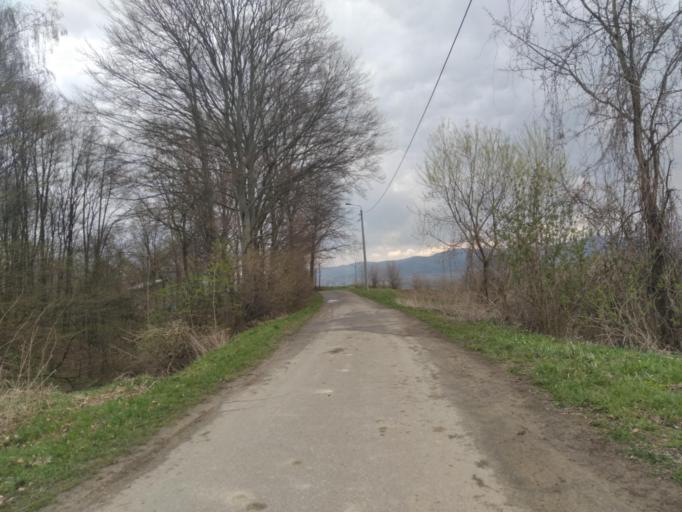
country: PL
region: Subcarpathian Voivodeship
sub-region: Powiat strzyzowski
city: Wisniowa
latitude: 49.8797
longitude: 21.6901
